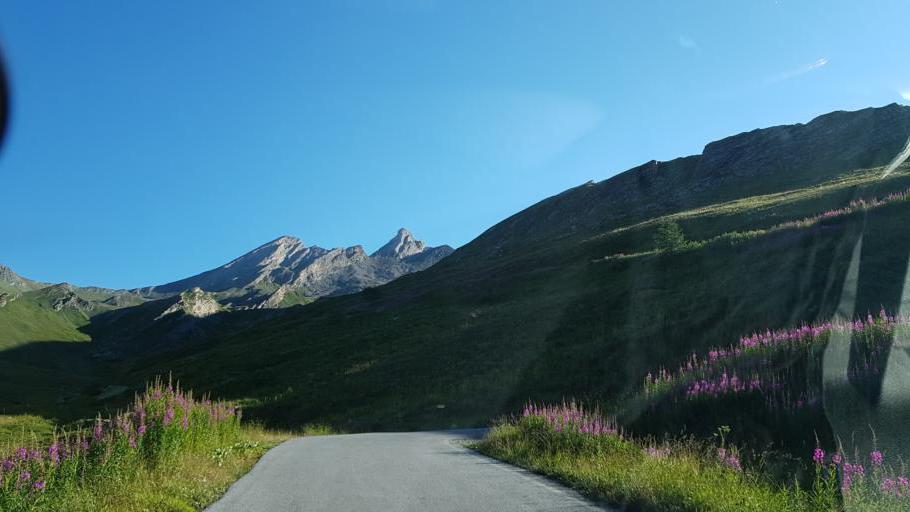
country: IT
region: Piedmont
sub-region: Provincia di Cuneo
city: Pontechianale
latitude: 44.6624
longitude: 6.9861
